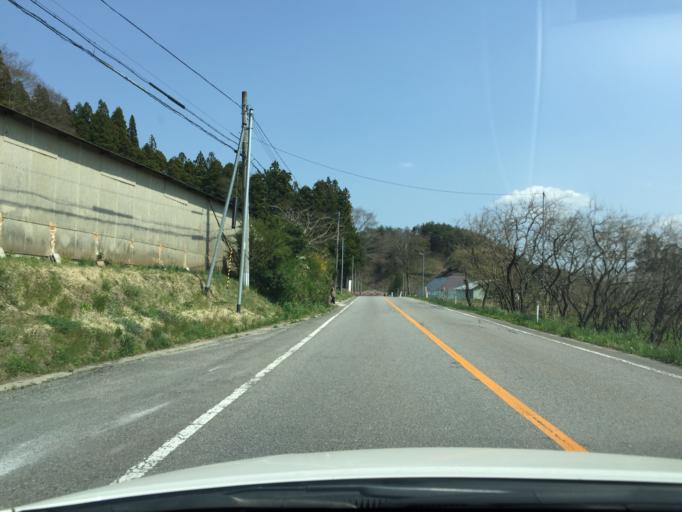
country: JP
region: Fukushima
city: Funehikimachi-funehiki
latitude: 37.4576
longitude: 140.7604
